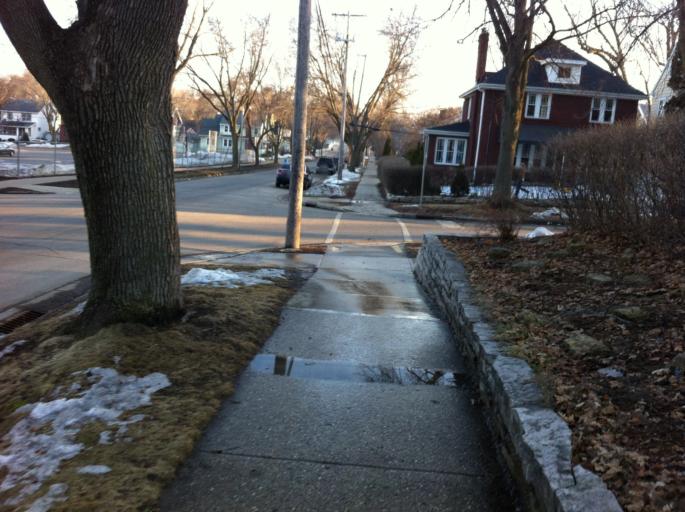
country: US
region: Wisconsin
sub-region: Dane County
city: Madison
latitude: 43.0672
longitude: -89.4239
